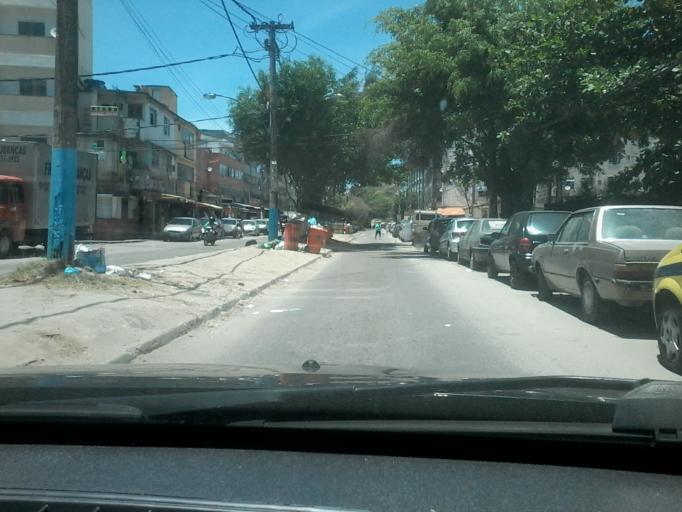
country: BR
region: Rio de Janeiro
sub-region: Nilopolis
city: Nilopolis
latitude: -23.0280
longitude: -43.4736
